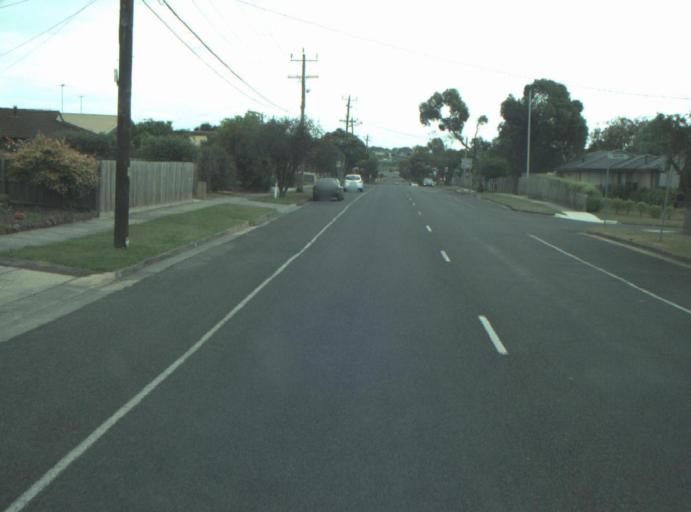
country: AU
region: Victoria
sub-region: Greater Geelong
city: Wandana Heights
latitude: -38.1860
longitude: 144.3232
